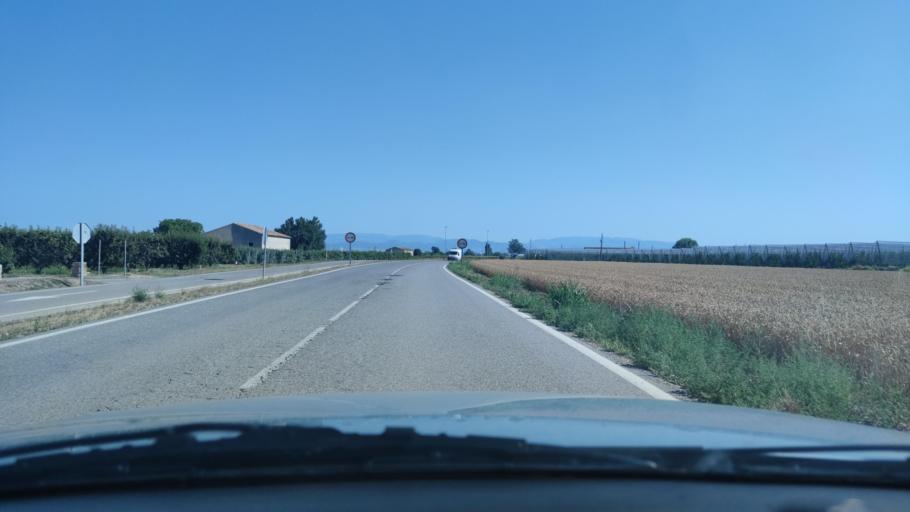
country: ES
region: Catalonia
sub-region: Provincia de Lleida
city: Bellvis
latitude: 41.6616
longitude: 0.8097
